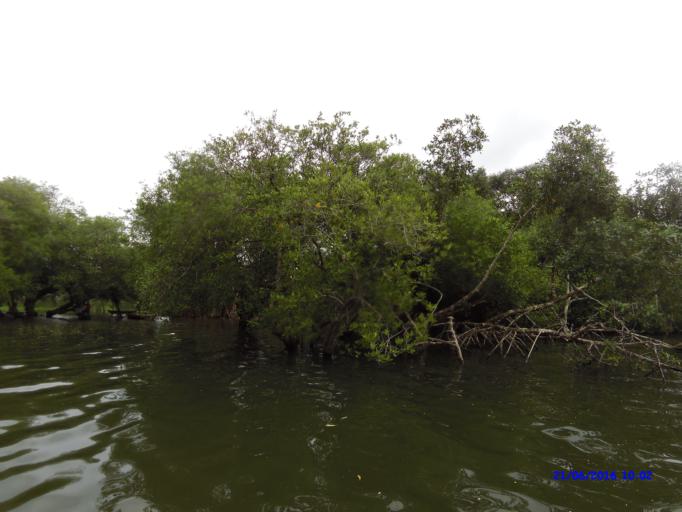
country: BJ
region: Mono
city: Come
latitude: 6.4542
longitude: 1.9252
